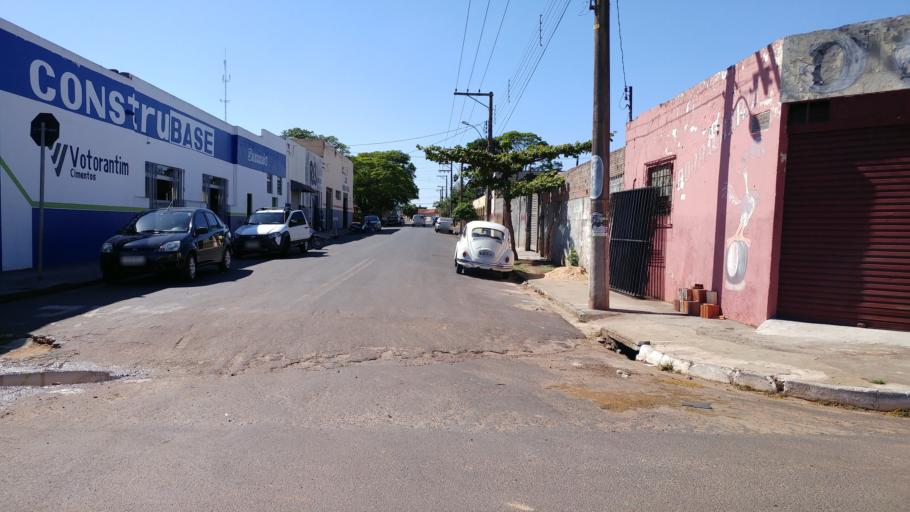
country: BR
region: Sao Paulo
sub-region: Paraguacu Paulista
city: Paraguacu Paulista
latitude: -22.4270
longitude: -50.5838
